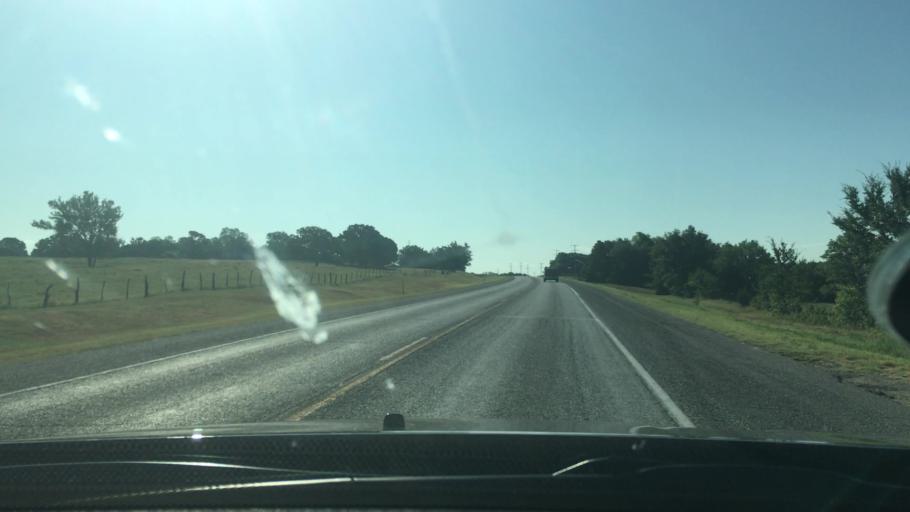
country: US
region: Oklahoma
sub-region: Johnston County
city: Tishomingo
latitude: 34.2387
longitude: -96.7370
